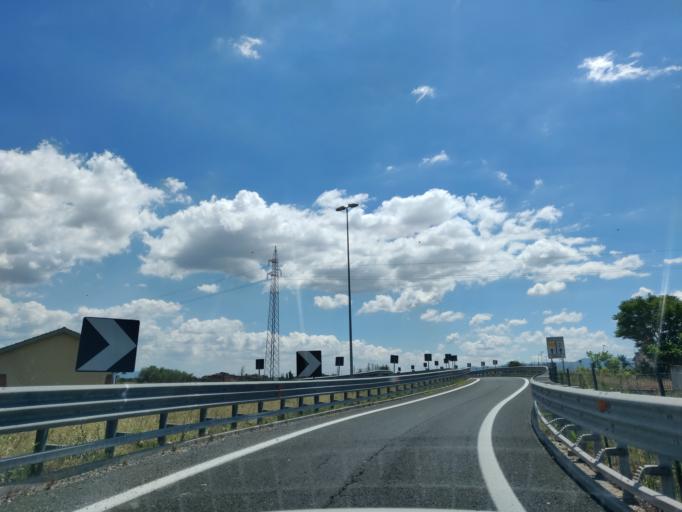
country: IT
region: Latium
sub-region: Citta metropolitana di Roma Capitale
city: Setteville
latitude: 41.9179
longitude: 12.6613
